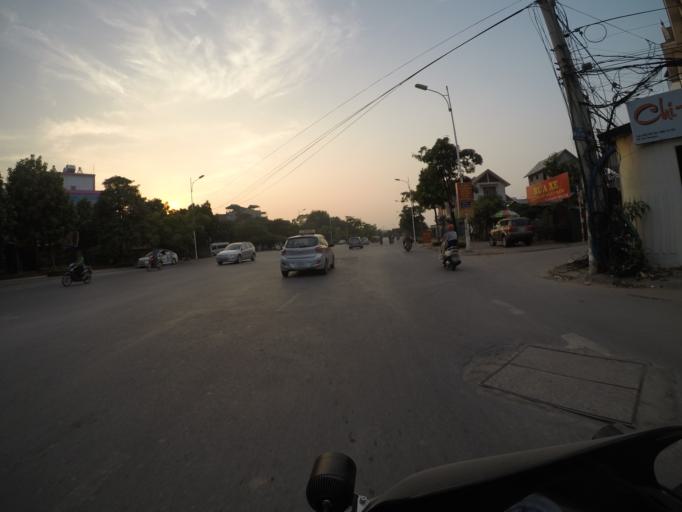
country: VN
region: Ha Noi
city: Hoan Kiem
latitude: 21.0292
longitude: 105.8857
